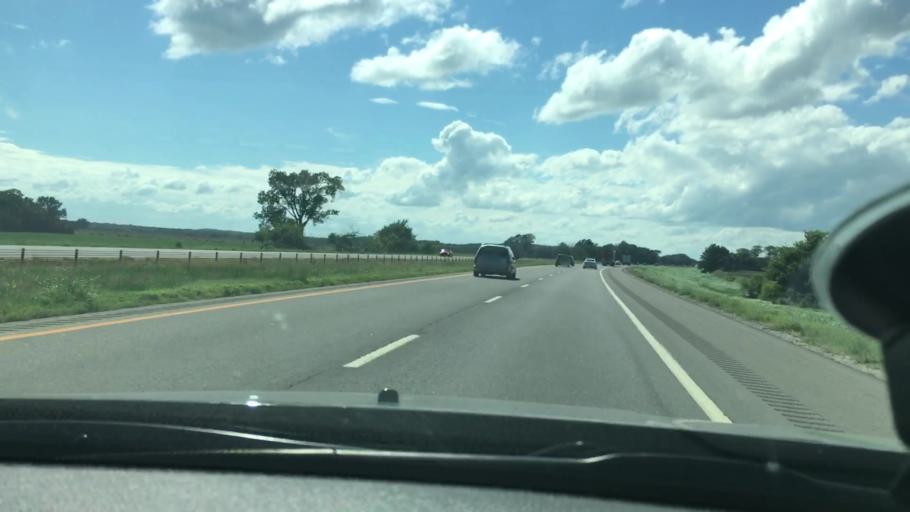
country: US
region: Oklahoma
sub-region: Sequoyah County
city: Vian
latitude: 35.4827
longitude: -95.1115
